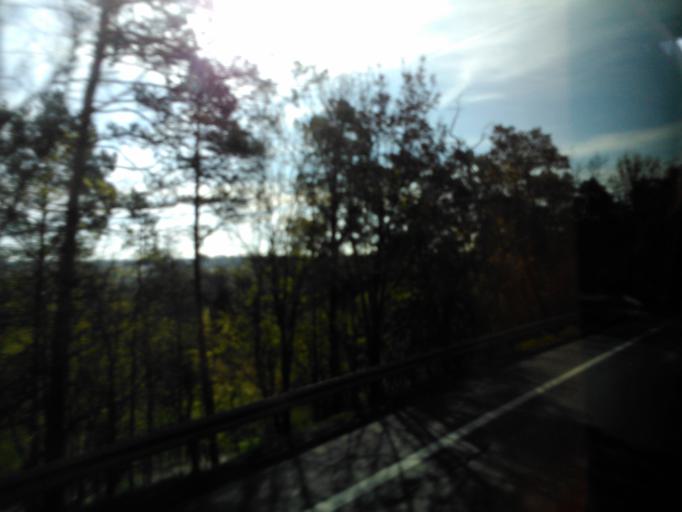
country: PL
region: Kujawsko-Pomorskie
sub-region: Powiat aleksandrowski
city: Aleksandrow Kujawski
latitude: 52.9606
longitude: 18.6865
